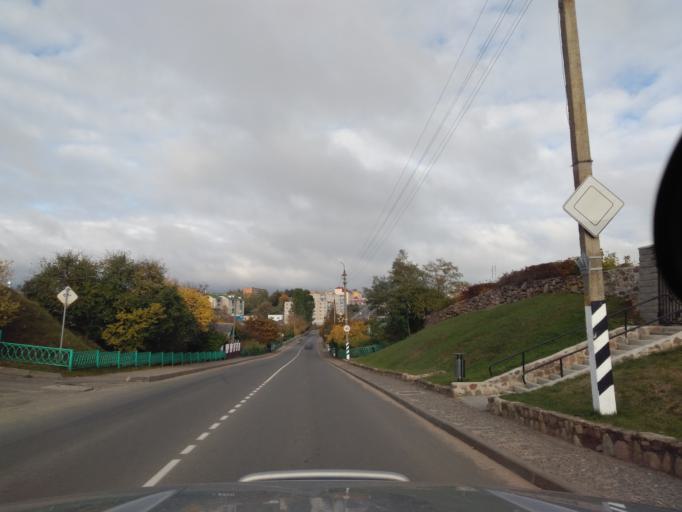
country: BY
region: Minsk
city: Kapyl'
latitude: 53.1467
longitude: 27.0976
